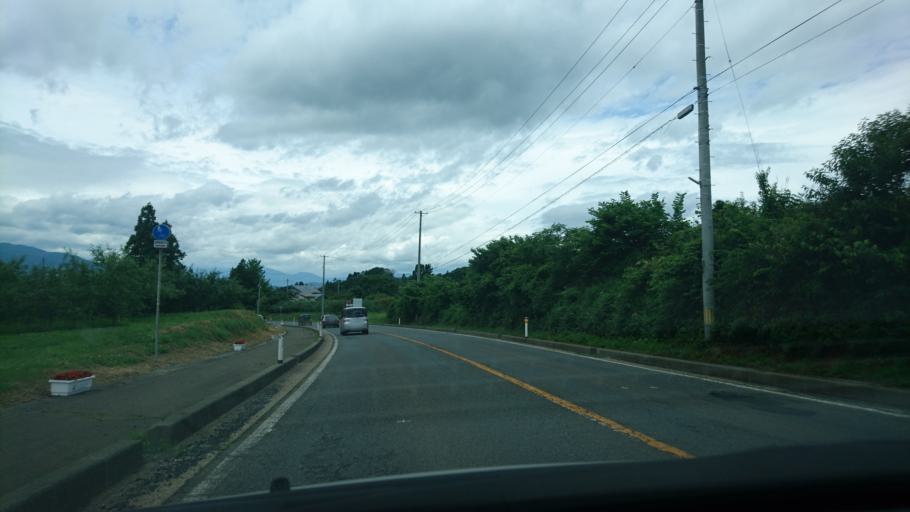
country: JP
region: Iwate
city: Morioka-shi
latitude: 39.6144
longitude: 141.1983
